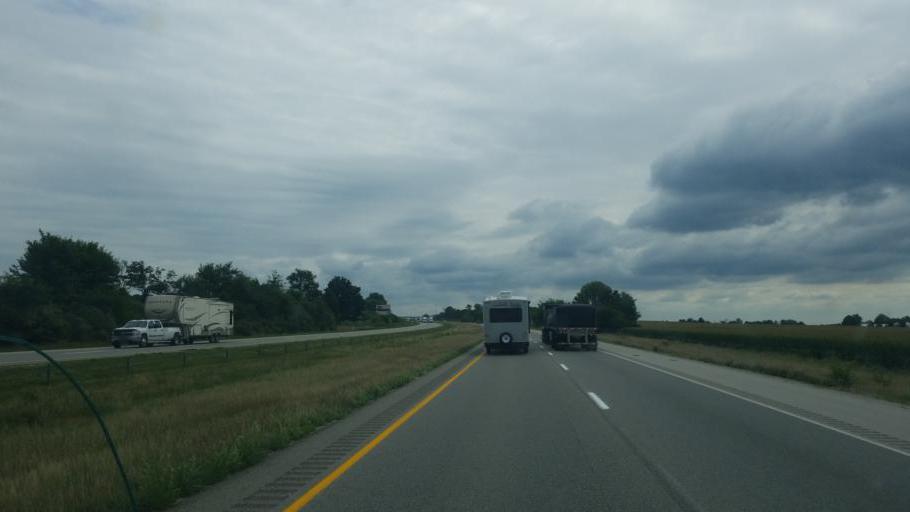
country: US
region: Indiana
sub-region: Morgan County
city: Monrovia
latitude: 39.5945
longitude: -86.5337
